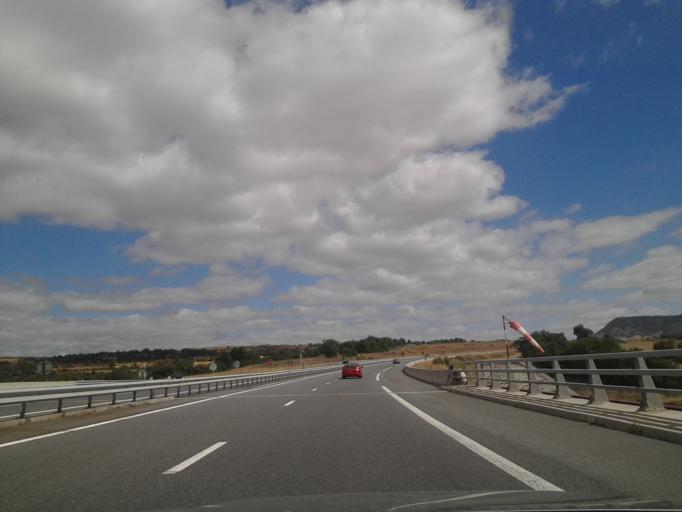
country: FR
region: Midi-Pyrenees
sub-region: Departement de l'Aveyron
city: Creissels
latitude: 44.0972
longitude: 3.0212
